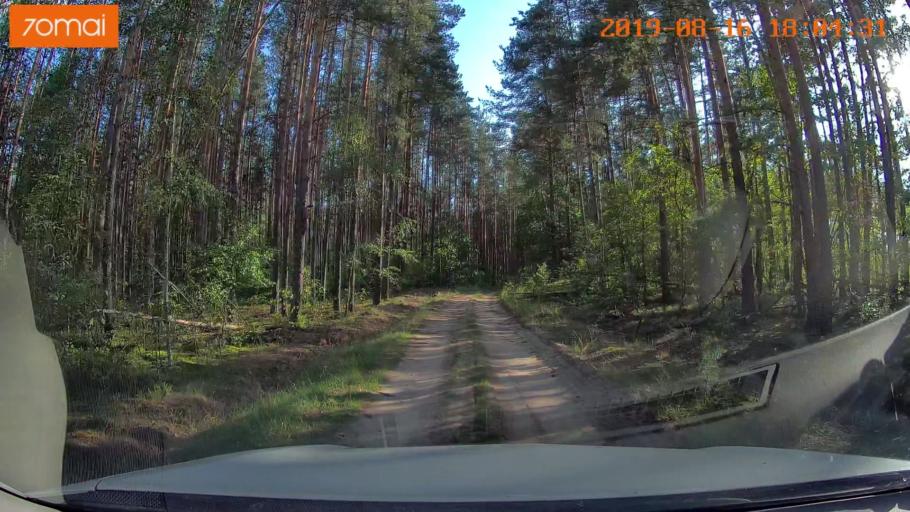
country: BY
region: Mogilev
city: Asipovichy
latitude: 53.2183
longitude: 28.6544
